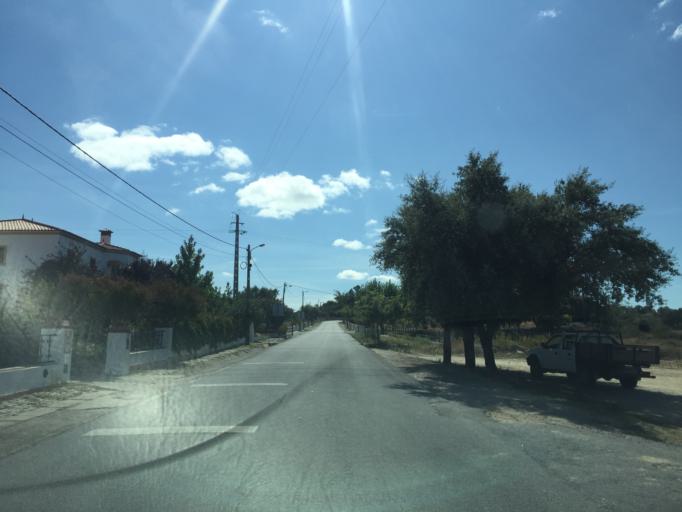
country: PT
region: Portalegre
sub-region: Marvao
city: Marvao
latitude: 39.4442
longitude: -7.3689
